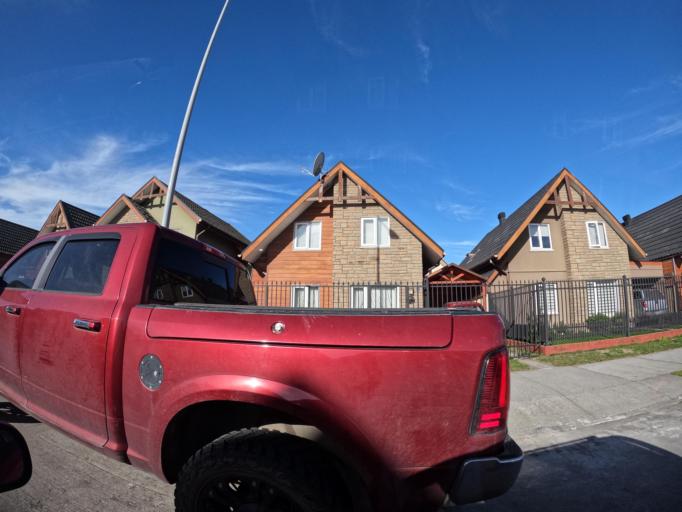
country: CL
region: Biobio
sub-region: Provincia de Concepcion
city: Concepcion
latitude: -36.7701
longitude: -73.0683
